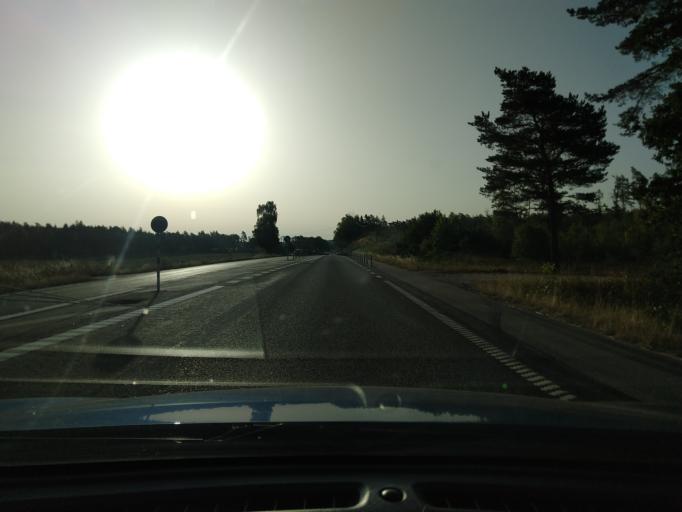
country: SE
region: Blekinge
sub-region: Karlskrona Kommun
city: Nattraby
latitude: 56.1988
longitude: 15.4152
